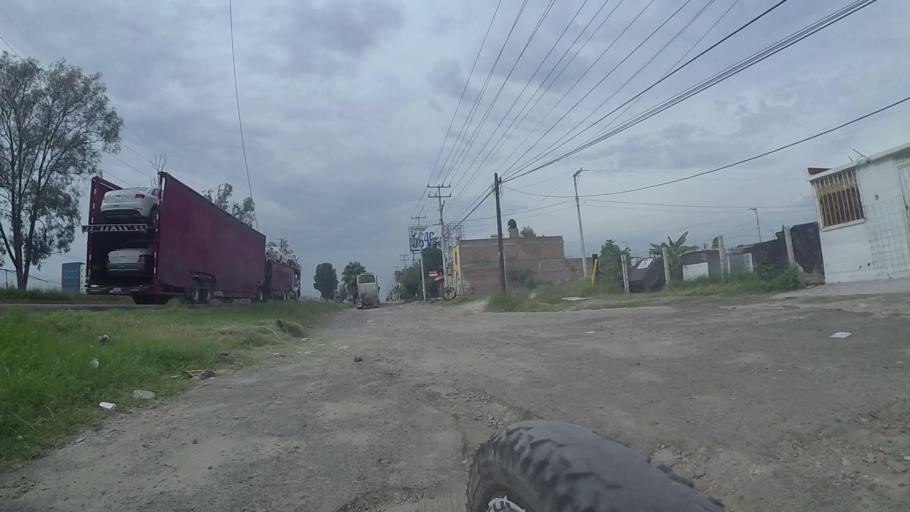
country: MX
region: Aguascalientes
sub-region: Aguascalientes
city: Penuelas (El Cienegal)
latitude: 21.7274
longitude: -102.2765
